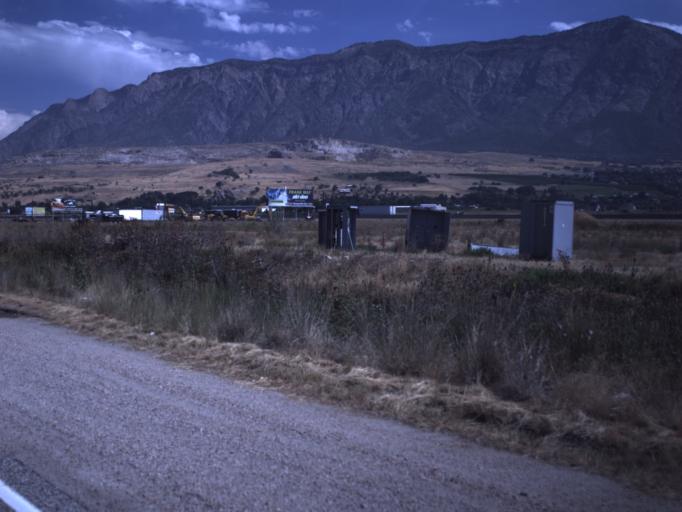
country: US
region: Utah
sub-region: Weber County
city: Farr West
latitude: 41.3145
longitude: -112.0279
